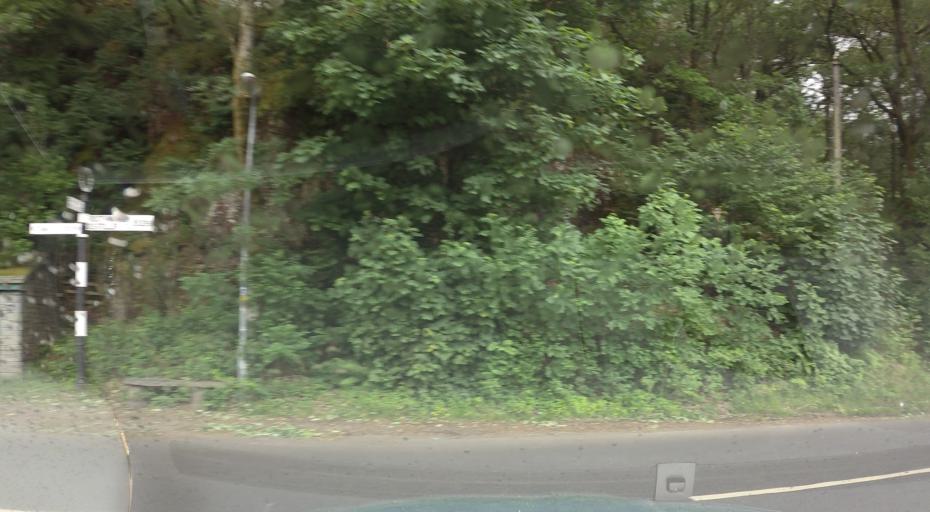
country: GB
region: England
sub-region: Cumbria
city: Keswick
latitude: 54.5467
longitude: -3.1541
